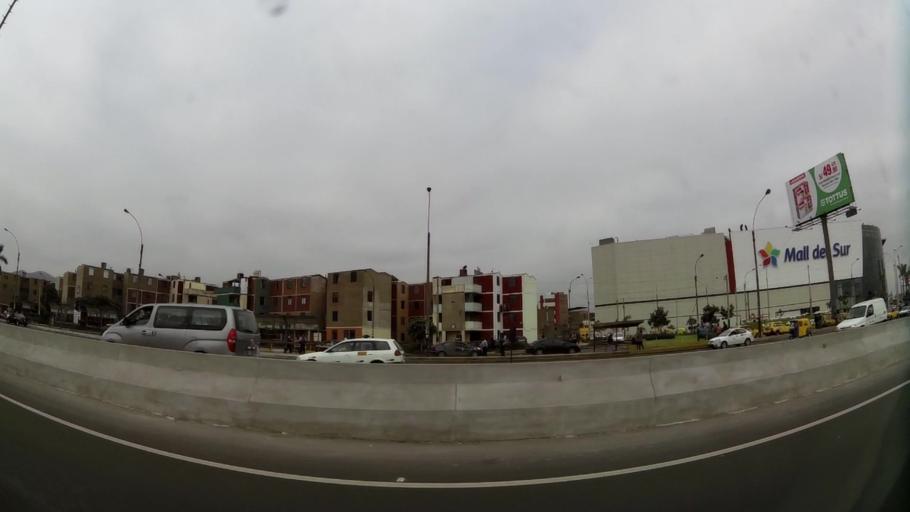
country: PE
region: Lima
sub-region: Lima
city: Surco
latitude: -12.1532
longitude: -76.9839
